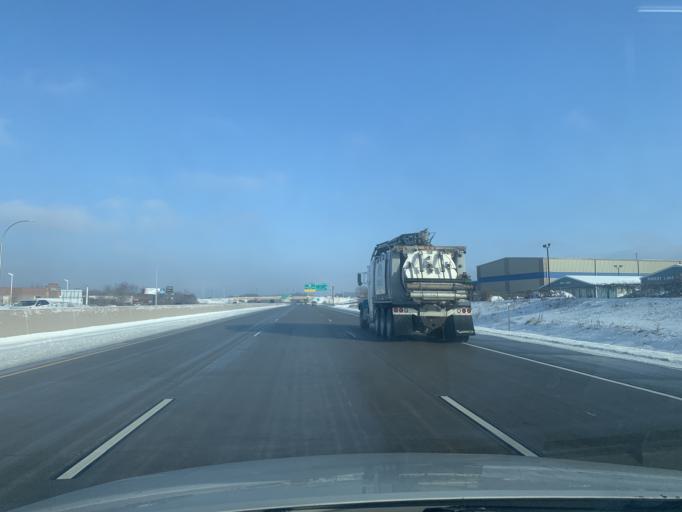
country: US
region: Minnesota
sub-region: Washington County
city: Forest Lake
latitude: 45.2745
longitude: -93.0055
